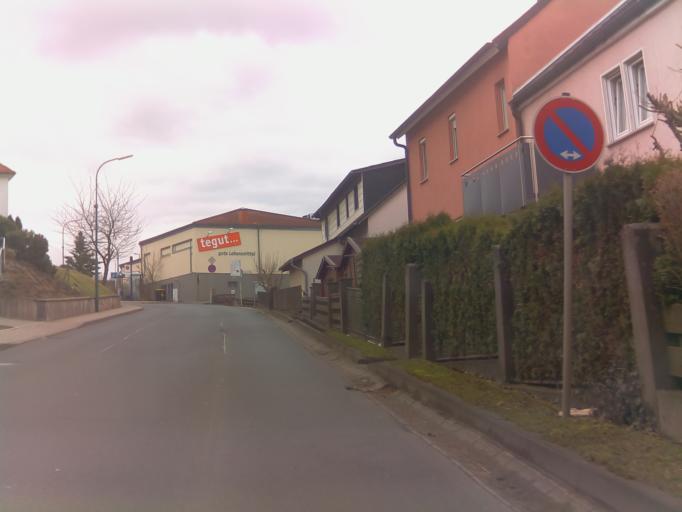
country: DE
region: Hesse
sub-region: Regierungsbezirk Kassel
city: Bad Salzschlirf
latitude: 50.6220
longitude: 9.5116
